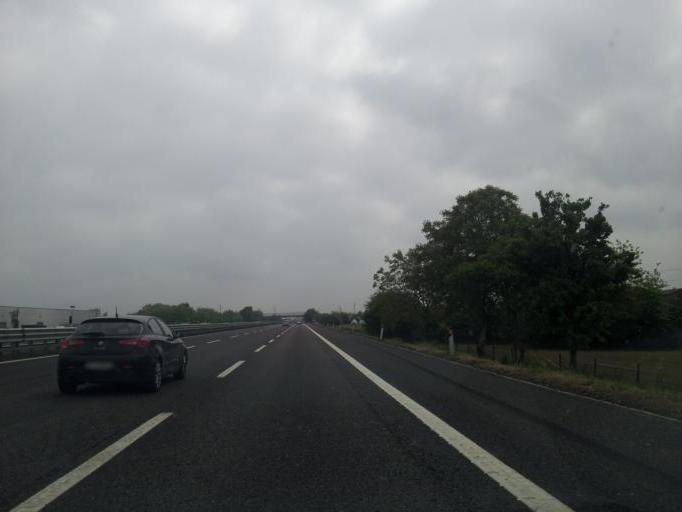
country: IT
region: Veneto
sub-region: Provincia di Padova
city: Taggi
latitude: 45.4534
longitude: 11.8107
